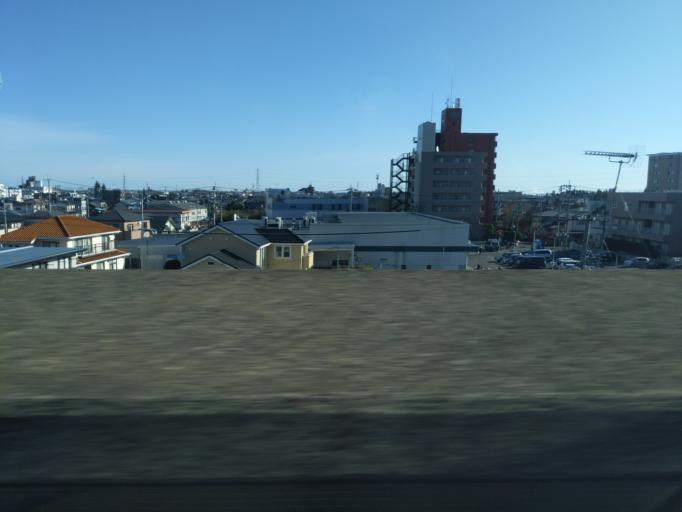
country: JP
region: Miyagi
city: Sendai
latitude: 38.1993
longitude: 140.8812
